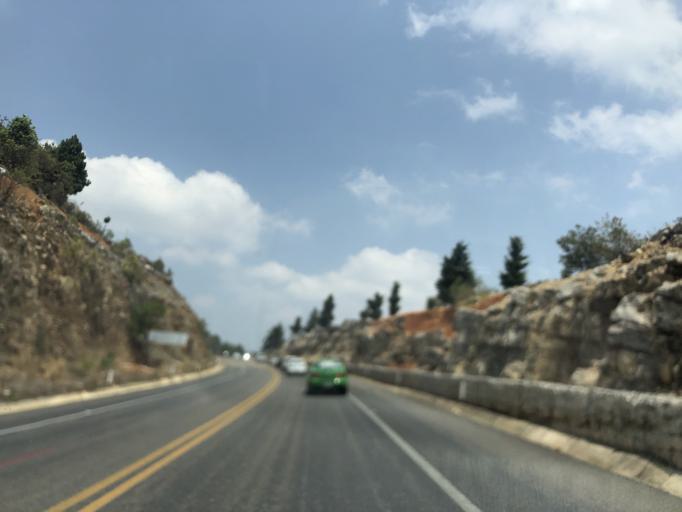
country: MX
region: Chiapas
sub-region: Zinacantan
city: Nachig
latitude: 16.6877
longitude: -92.7215
